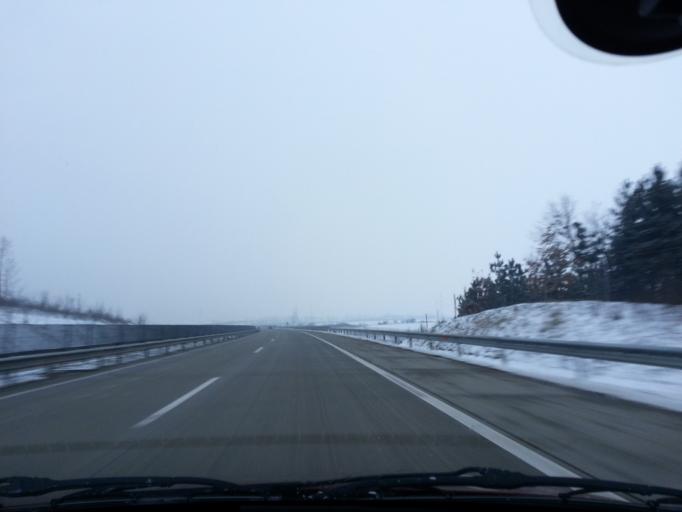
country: HU
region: Pest
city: Kerepes
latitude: 47.5621
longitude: 19.3197
